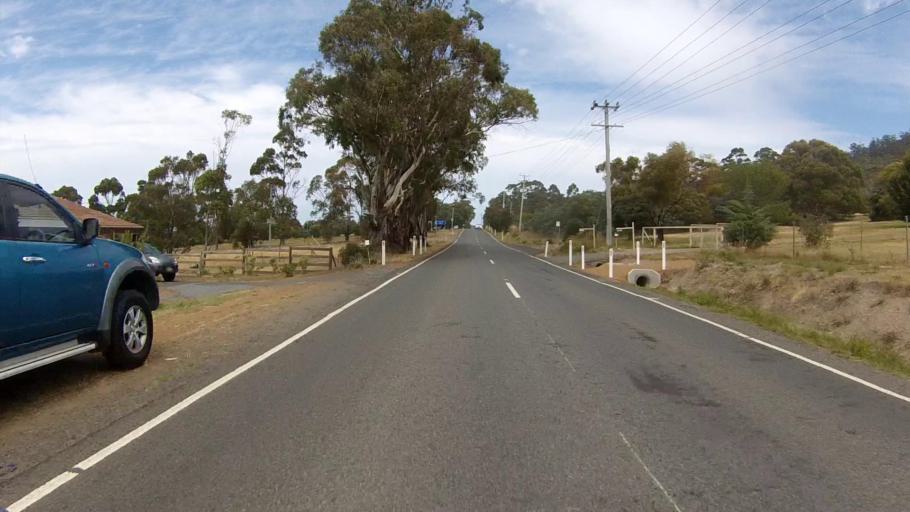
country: AU
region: Tasmania
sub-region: Clarence
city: Acton Park
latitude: -42.8948
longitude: 147.4814
